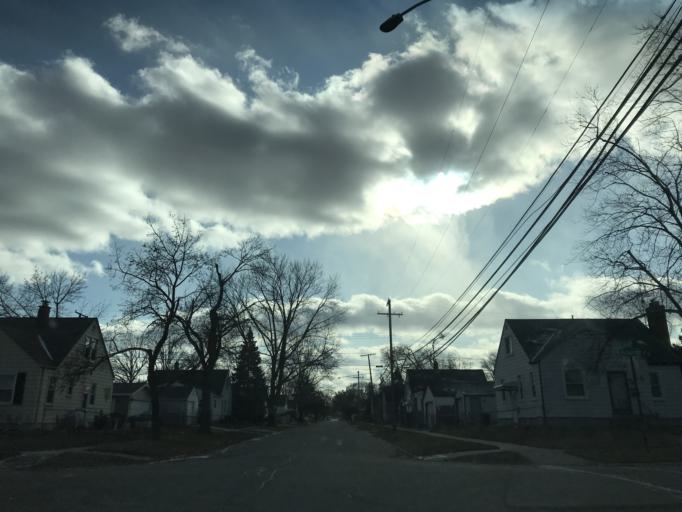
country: US
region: Michigan
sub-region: Oakland County
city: Madison Heights
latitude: 42.4753
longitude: -83.1165
